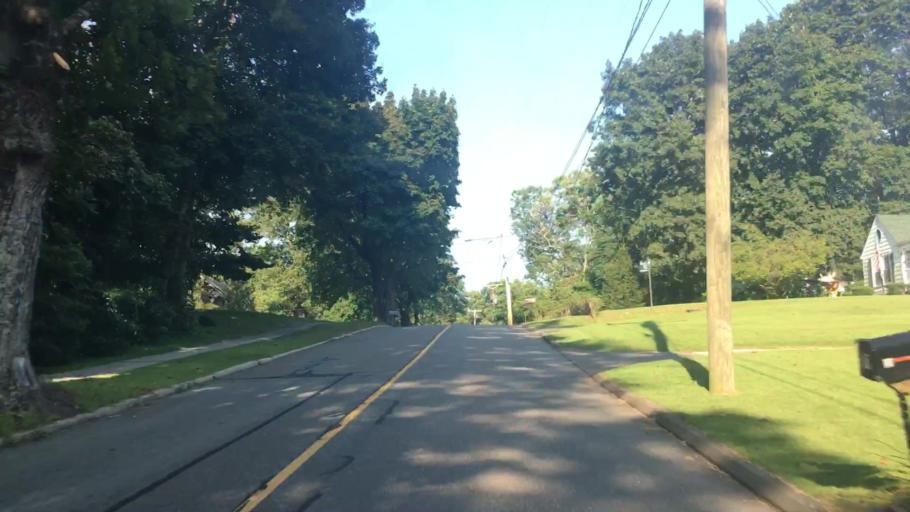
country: US
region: Connecticut
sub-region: Middlesex County
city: Chester Center
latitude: 41.4045
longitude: -72.4598
